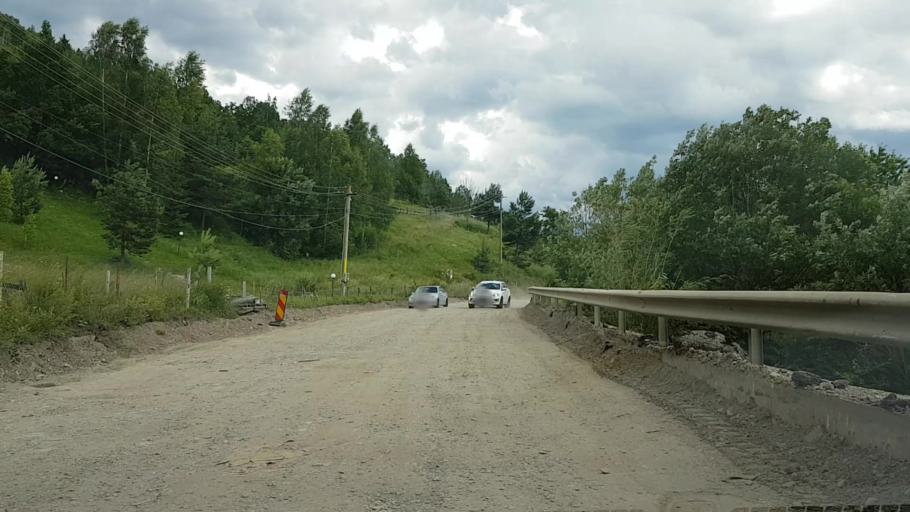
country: RO
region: Neamt
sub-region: Comuna Hangu
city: Hangu
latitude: 47.0384
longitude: 26.0585
